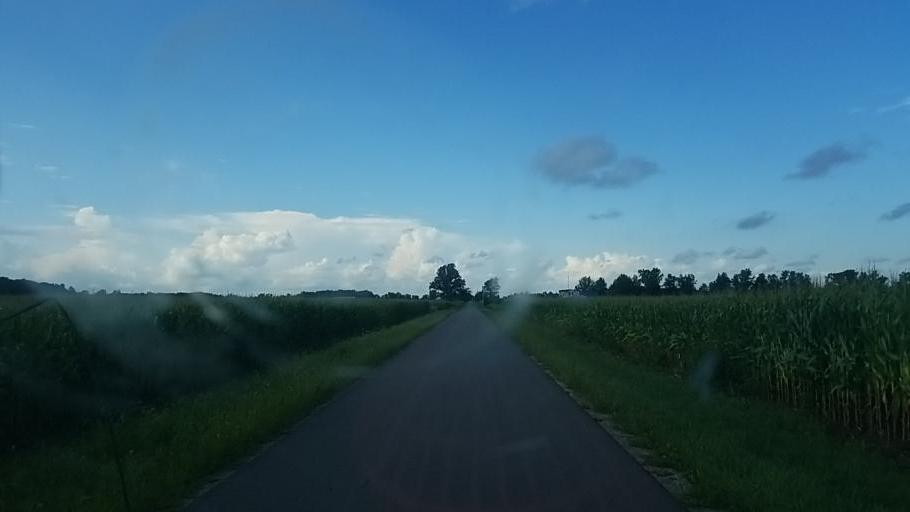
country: US
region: Ohio
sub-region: Hardin County
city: Forest
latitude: 40.7803
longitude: -83.4485
